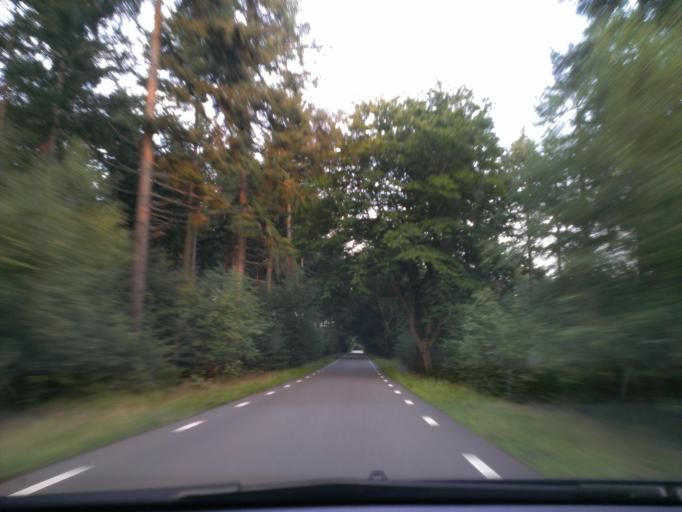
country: NL
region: Gelderland
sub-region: Gemeente Epe
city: Epe
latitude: 52.3939
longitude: 5.9779
